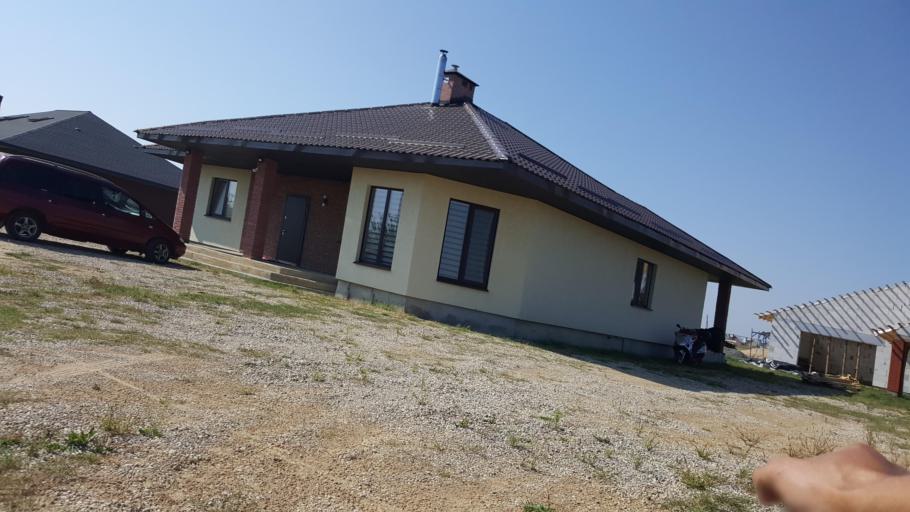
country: BY
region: Brest
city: Vysokaye
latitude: 52.4144
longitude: 23.4672
